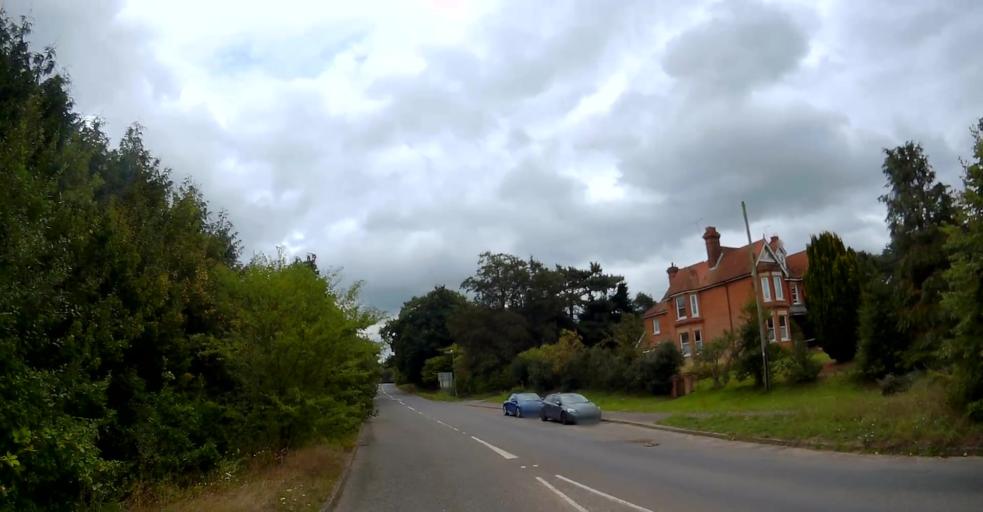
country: GB
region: England
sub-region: Surrey
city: Hale
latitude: 51.2208
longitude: -0.7672
